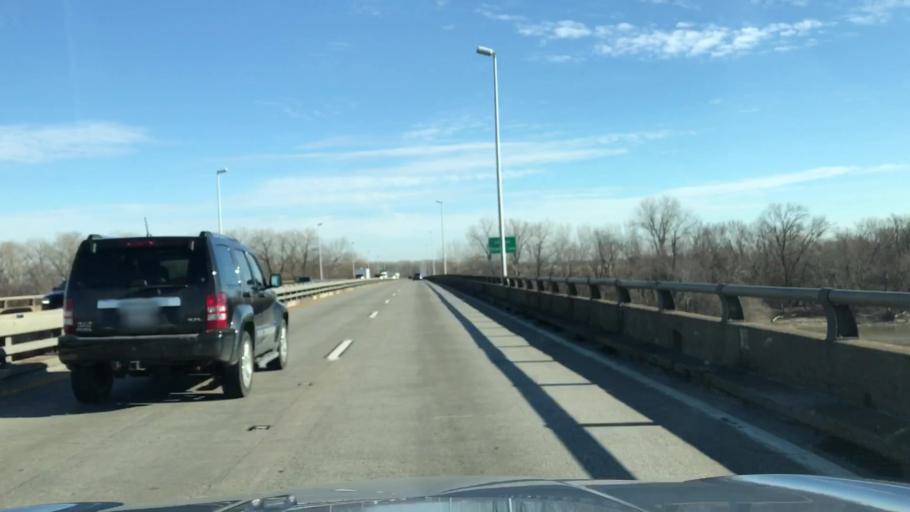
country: US
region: Missouri
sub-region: Saint Louis County
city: Glasgow Village
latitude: 38.7639
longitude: -90.1705
